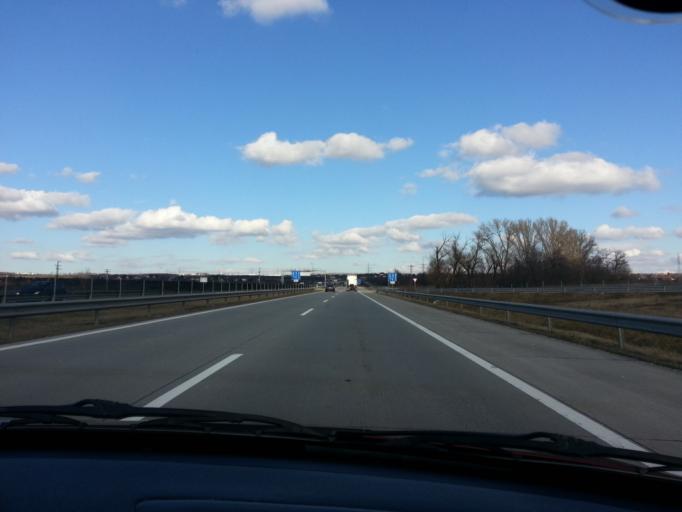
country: HU
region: Pest
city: Ecser
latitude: 47.4322
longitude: 19.3274
